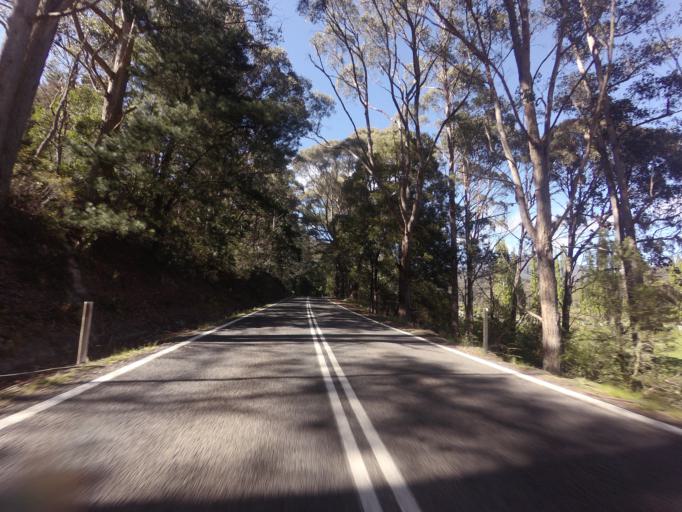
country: AU
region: Tasmania
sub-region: Derwent Valley
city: New Norfolk
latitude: -42.6990
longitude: 146.7137
